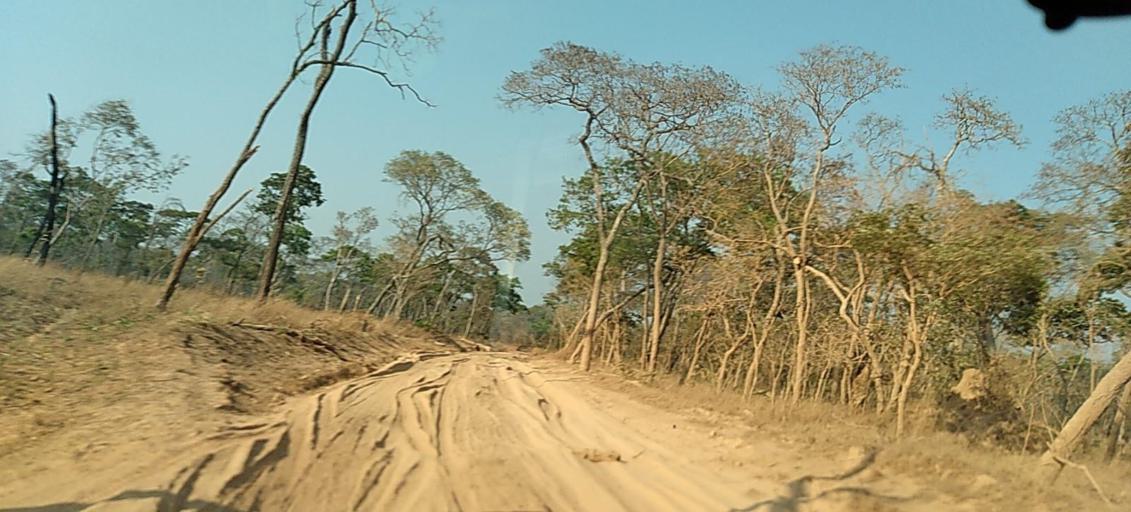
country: ZM
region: North-Western
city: Kasempa
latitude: -13.5723
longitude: 25.9934
